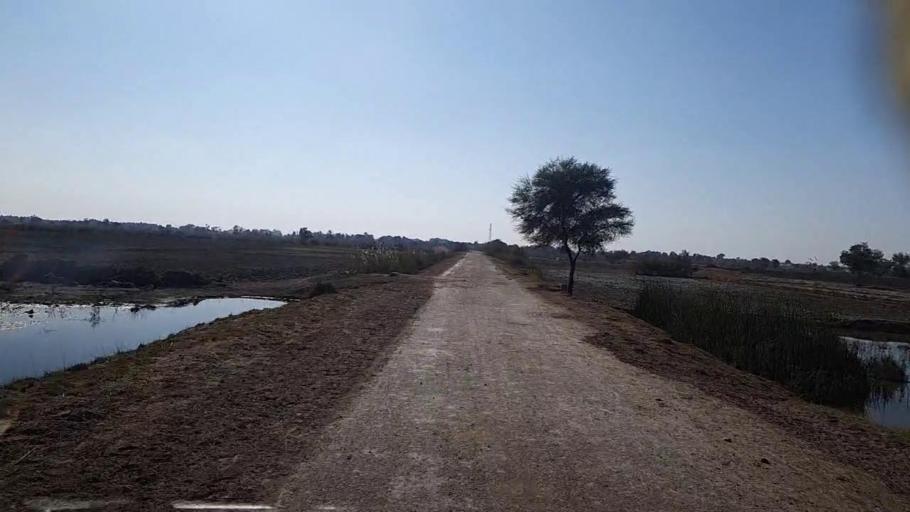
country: PK
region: Sindh
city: Khairpur
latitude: 27.9450
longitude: 69.7289
